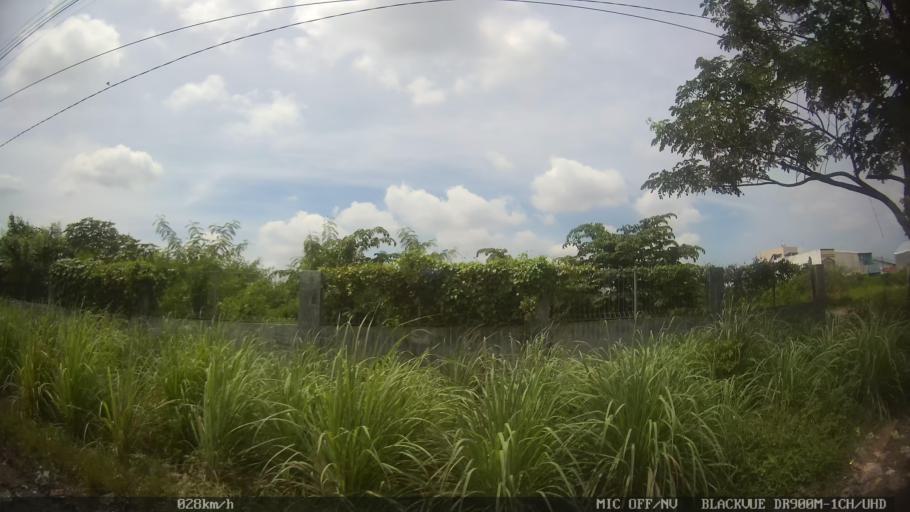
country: ID
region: North Sumatra
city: Medan
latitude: 3.6425
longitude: 98.6872
